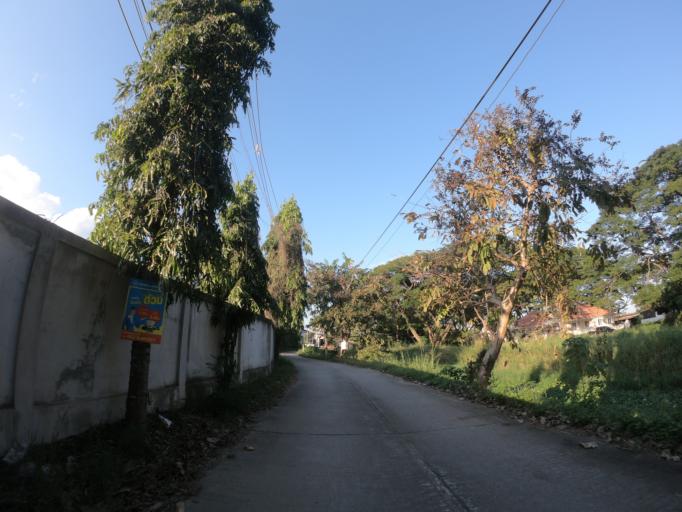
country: TH
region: Chiang Mai
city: Chiang Mai
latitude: 18.7395
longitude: 98.9780
